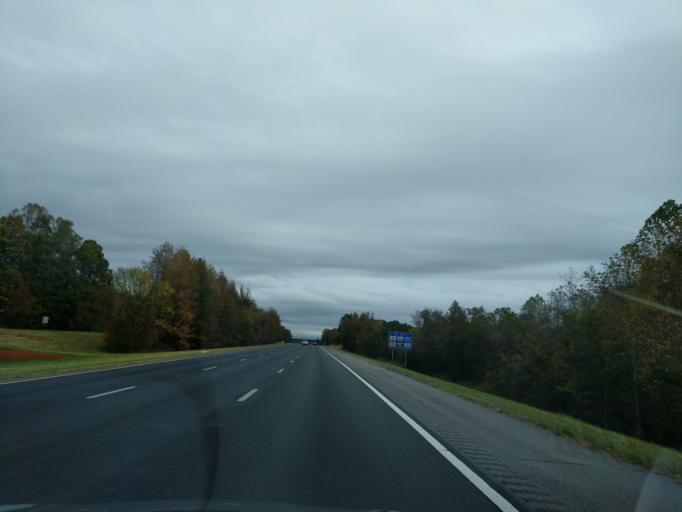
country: US
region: North Carolina
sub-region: Davidson County
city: Lexington
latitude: 35.7775
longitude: -80.2692
